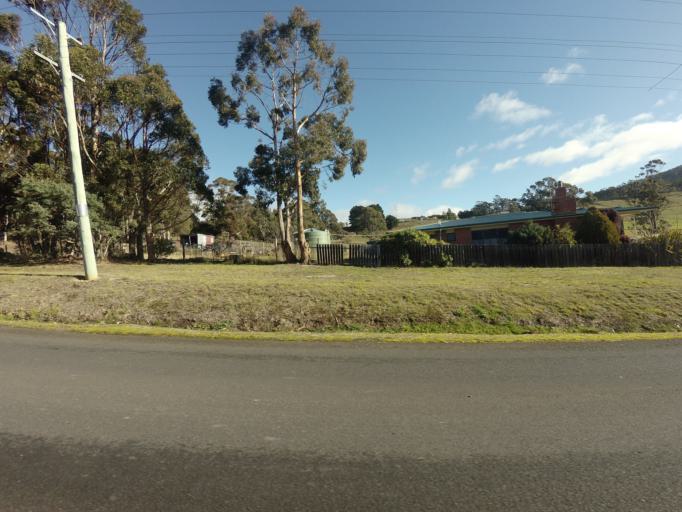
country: AU
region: Tasmania
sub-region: Glenorchy
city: Berriedale
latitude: -42.8232
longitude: 147.2039
